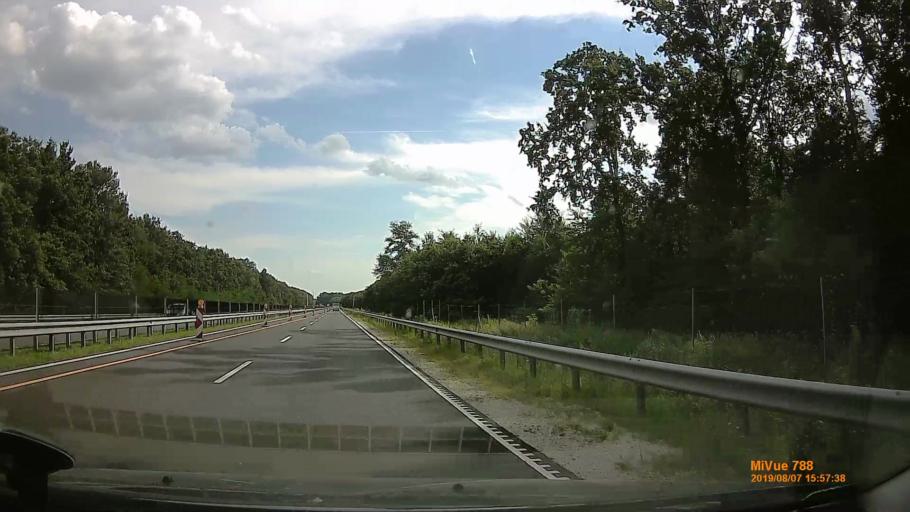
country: HU
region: Vas
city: Kormend
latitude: 47.0384
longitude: 16.6133
